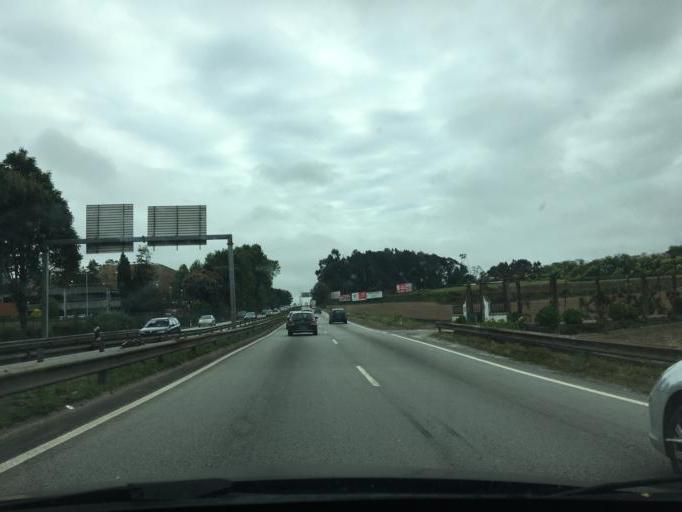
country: PT
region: Porto
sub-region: Maia
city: Leca do Bailio
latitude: 41.2164
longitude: -8.6271
